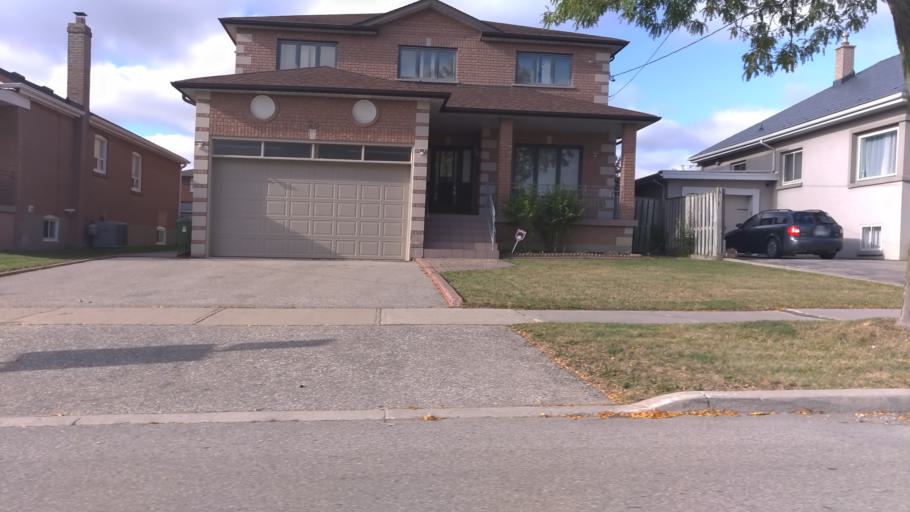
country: CA
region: Ontario
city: Toronto
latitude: 43.7214
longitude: -79.4585
